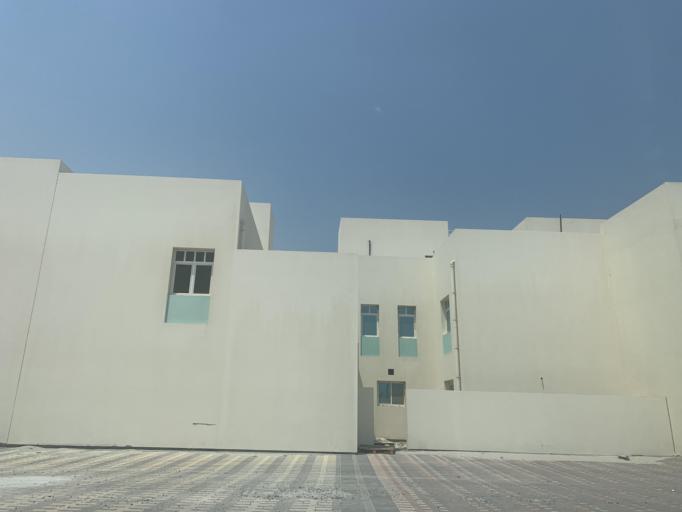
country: BH
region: Muharraq
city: Al Hadd
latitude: 26.2412
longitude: 50.6673
